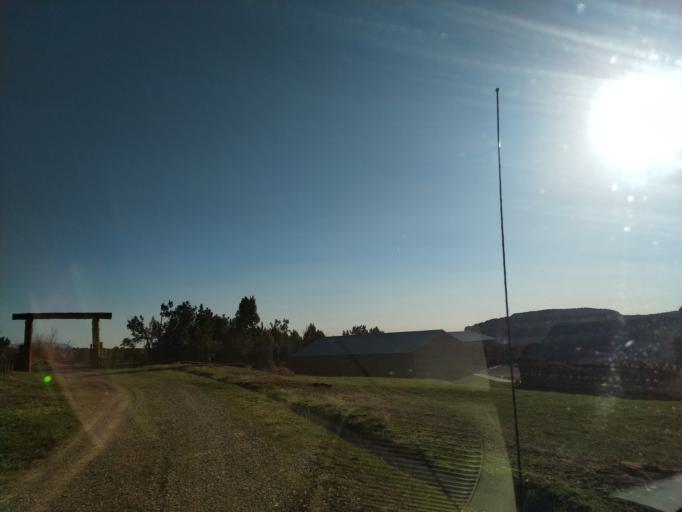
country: US
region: Colorado
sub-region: Mesa County
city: Loma
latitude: 38.9544
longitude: -109.0604
